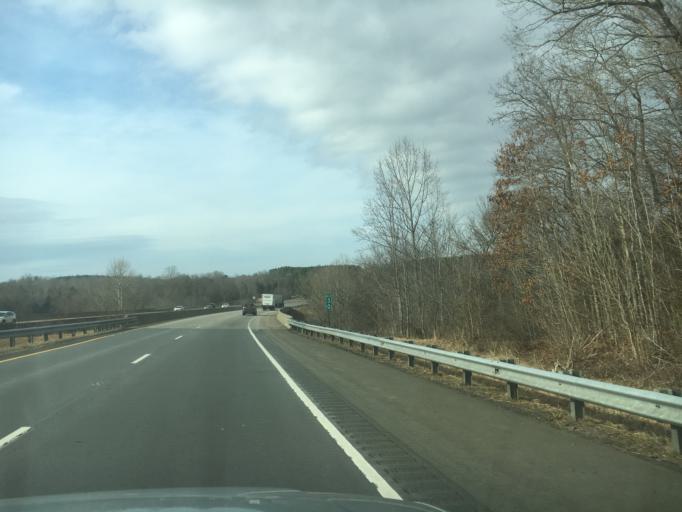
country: US
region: North Carolina
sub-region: Catawba County
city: Maiden
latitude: 35.5562
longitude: -81.2446
